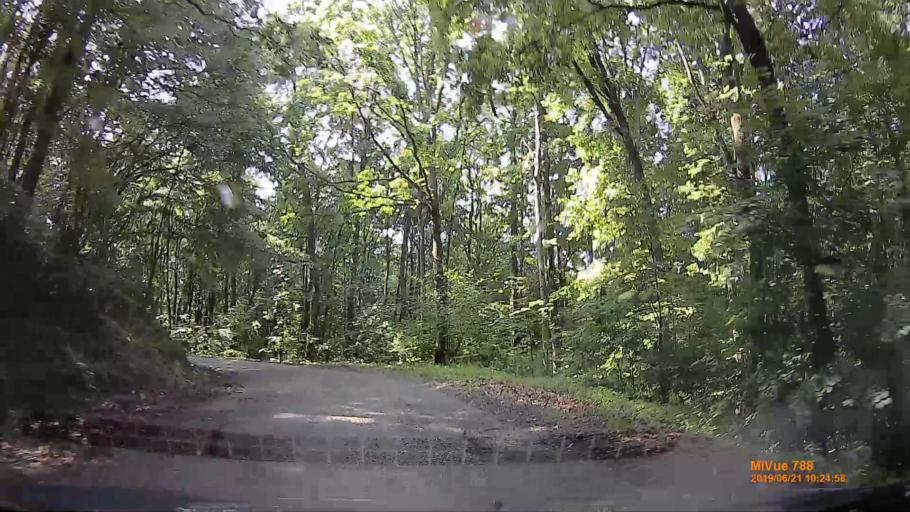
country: HU
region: Baranya
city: Buekkoesd
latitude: 46.1810
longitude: 17.9745
